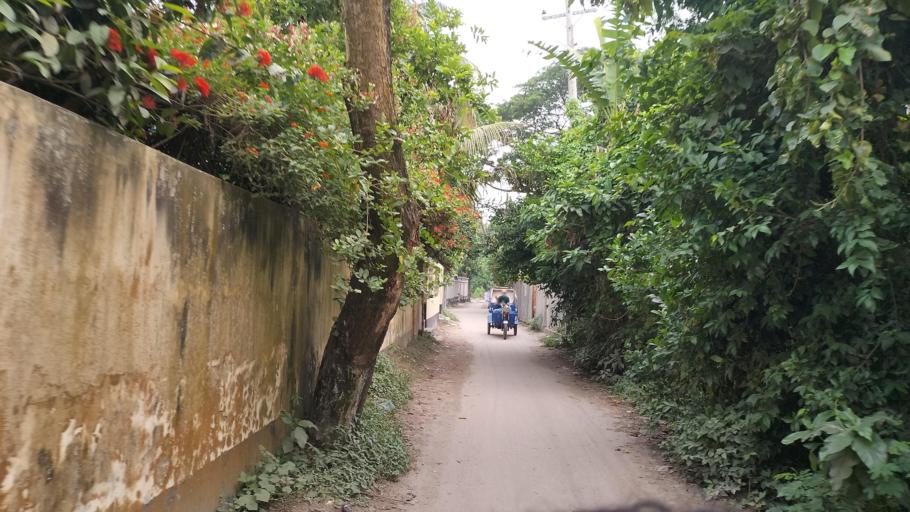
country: BD
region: Dhaka
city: Azimpur
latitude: 23.6801
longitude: 90.3149
